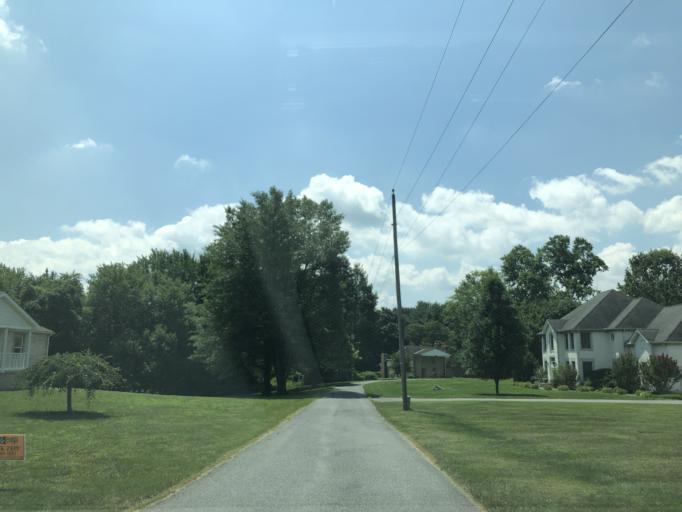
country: US
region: Maryland
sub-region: Carroll County
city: Westminster
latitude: 39.5297
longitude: -76.9391
